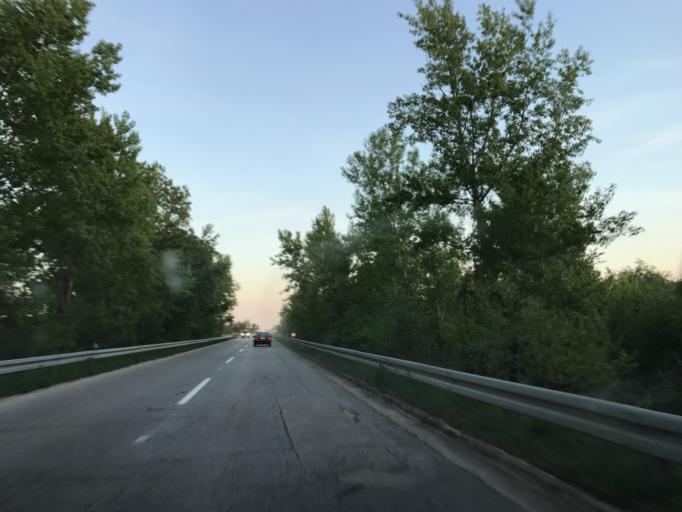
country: RS
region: Central Serbia
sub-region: Borski Okrug
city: Negotin
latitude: 44.2678
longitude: 22.5137
